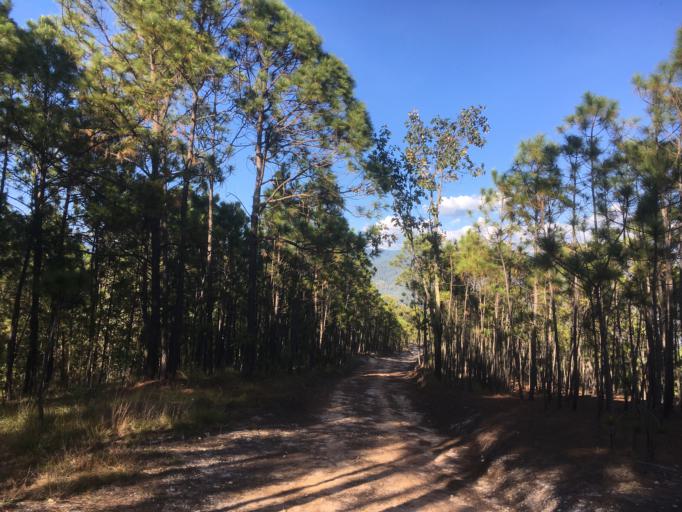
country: MX
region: Michoacan
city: Tzitzio
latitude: 19.6059
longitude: -100.9259
